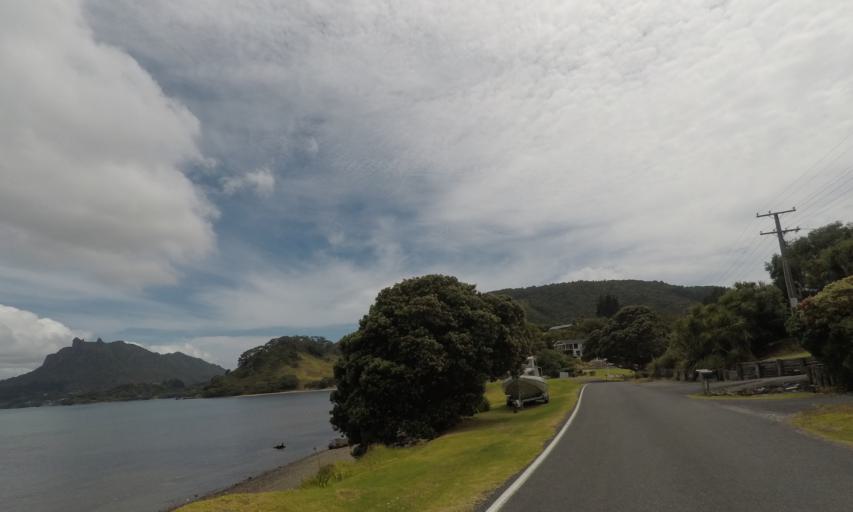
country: NZ
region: Northland
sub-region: Whangarei
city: Ruakaka
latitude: -35.8455
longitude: 174.5361
